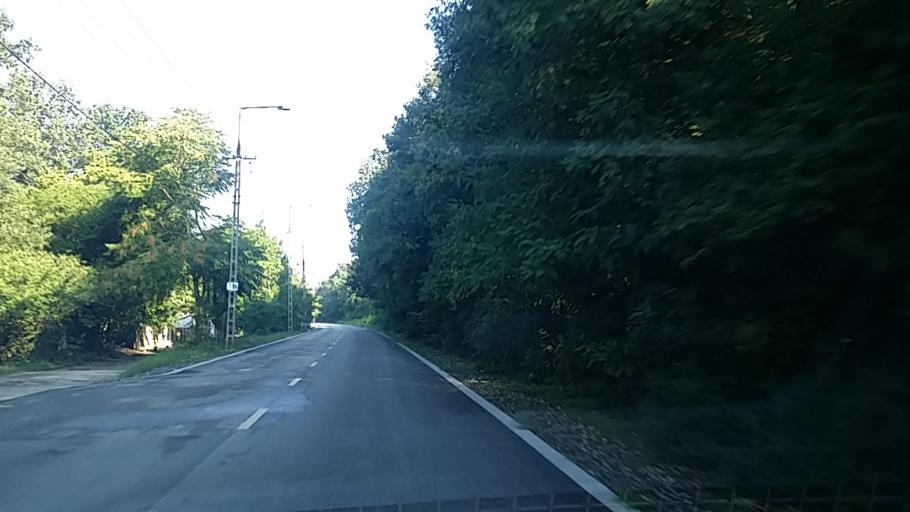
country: HU
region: Komarom-Esztergom
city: Tatabanya
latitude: 47.5829
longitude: 18.4142
